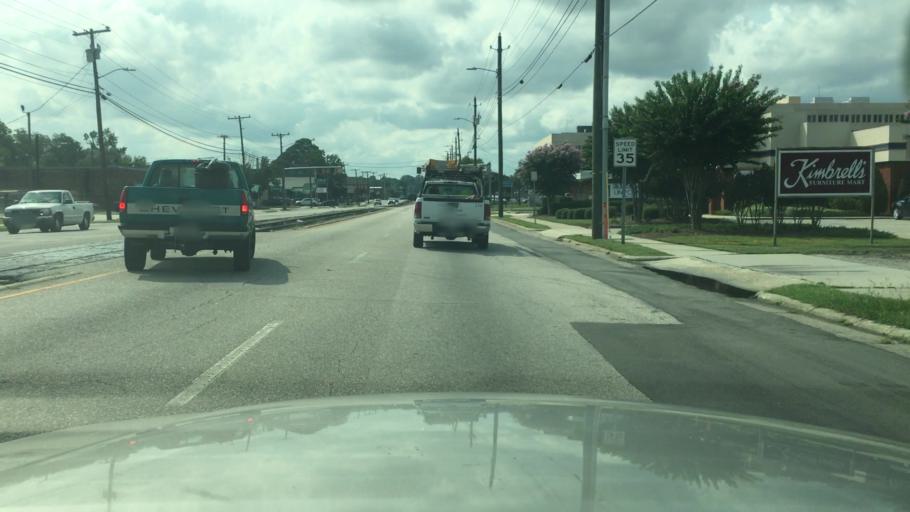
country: US
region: North Carolina
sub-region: Cumberland County
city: Fayetteville
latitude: 35.0489
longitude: -78.8740
